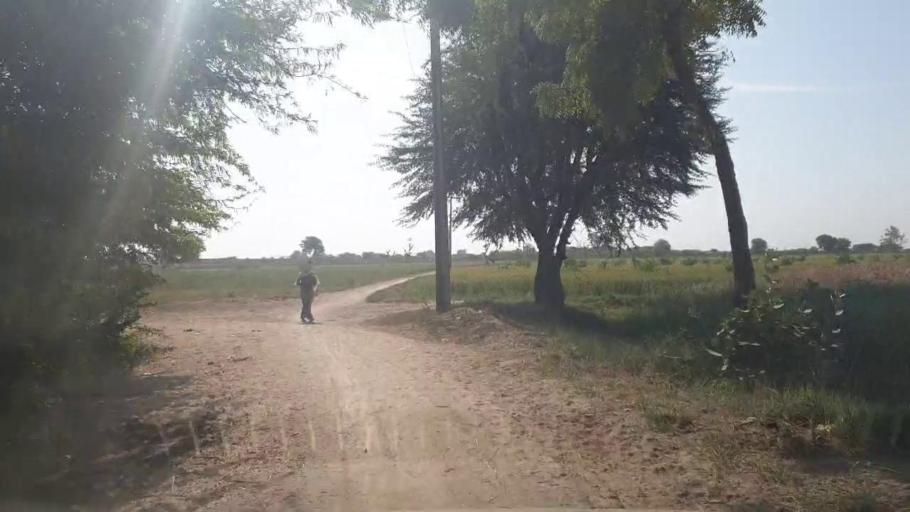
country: PK
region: Sindh
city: Umarkot
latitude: 25.2980
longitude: 69.6781
